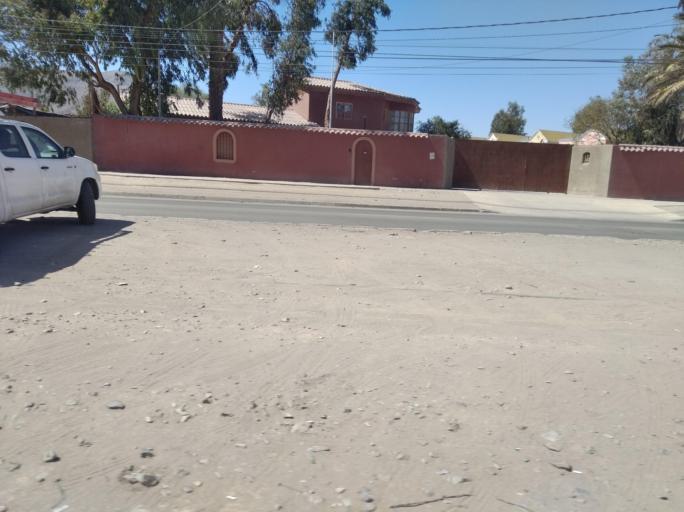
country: CL
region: Atacama
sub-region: Provincia de Copiapo
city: Copiapo
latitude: -27.3992
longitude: -70.2939
